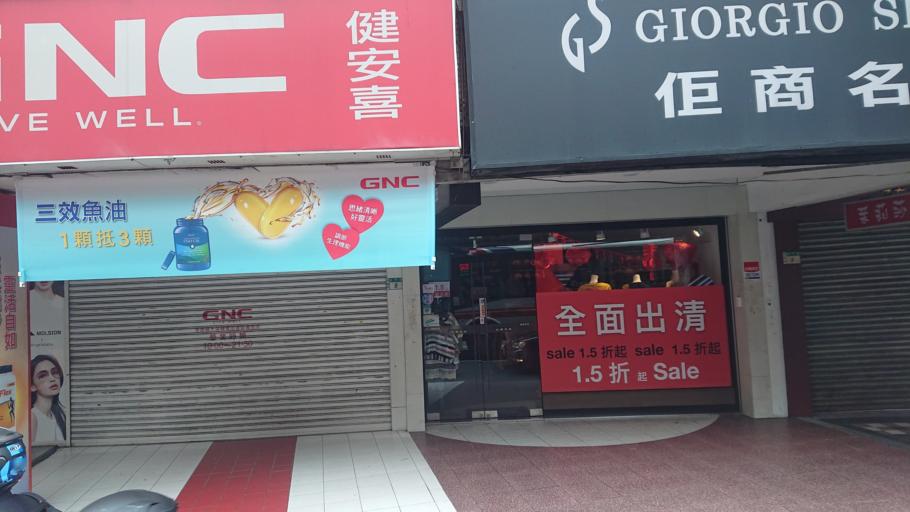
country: TW
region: Taipei
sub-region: Taipei
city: Banqiao
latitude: 25.0092
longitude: 121.4576
